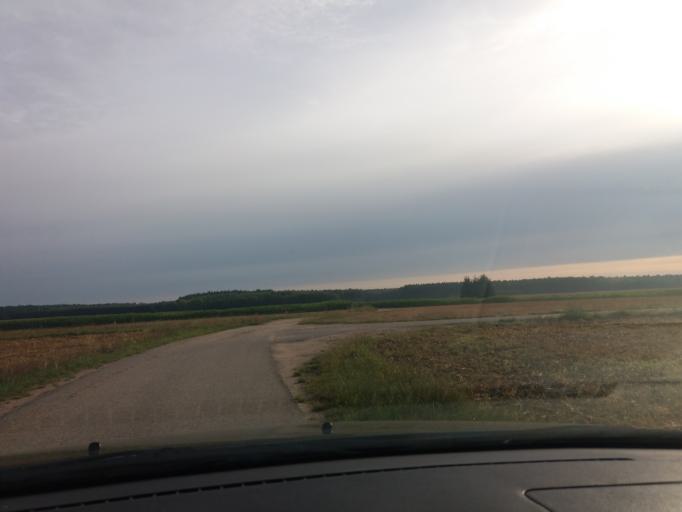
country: PL
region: Masovian Voivodeship
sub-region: Powiat mlawski
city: Wieczfnia Koscielna
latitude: 53.2115
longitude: 20.4535
